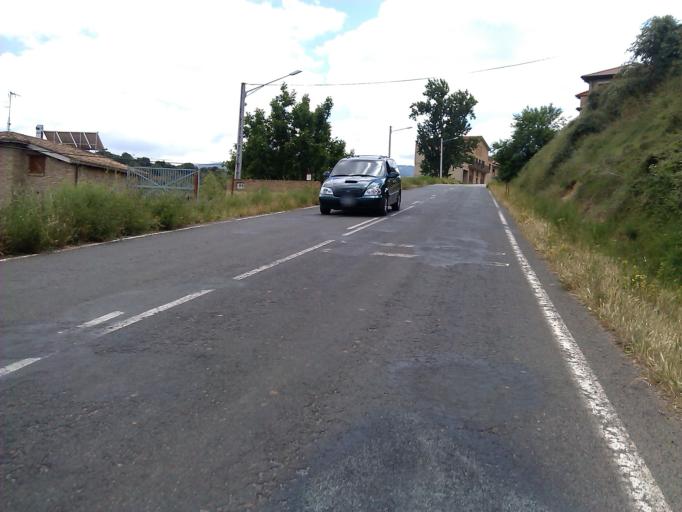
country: ES
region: La Rioja
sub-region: Provincia de La Rioja
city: Hornos de Moncalvillo
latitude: 42.4022
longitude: -2.6005
